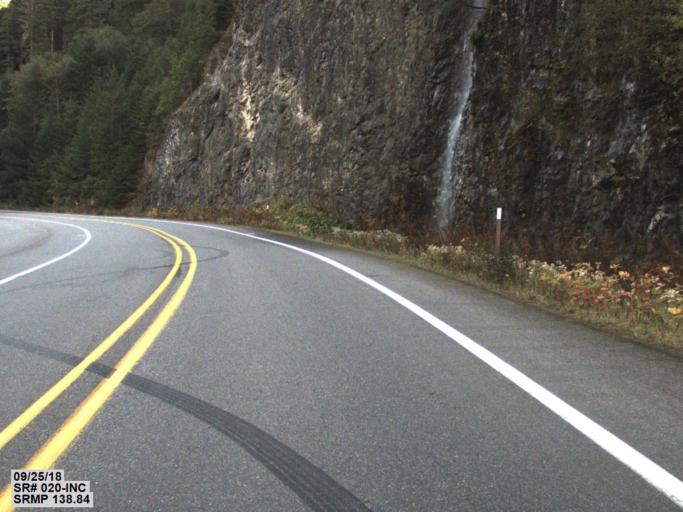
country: US
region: Washington
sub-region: Snohomish County
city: Darrington
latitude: 48.7054
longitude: -120.9690
